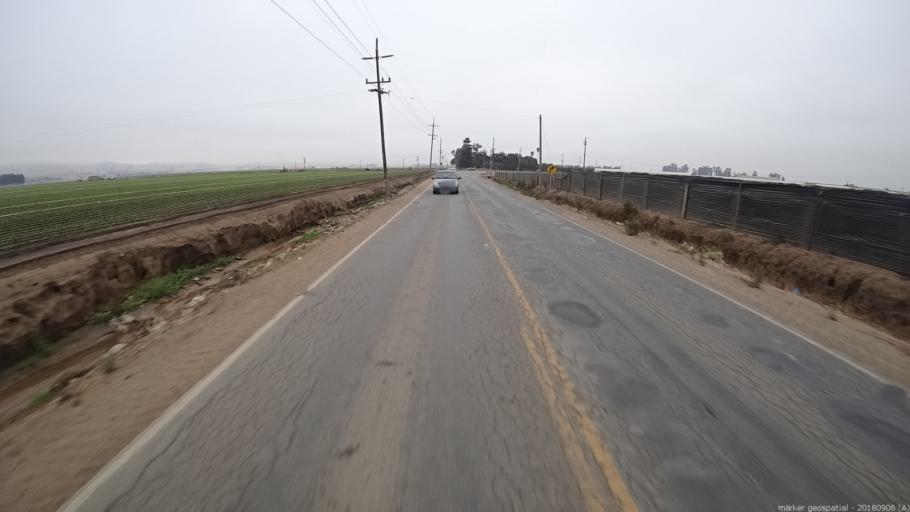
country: US
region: California
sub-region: Monterey County
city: Chualar
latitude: 36.6273
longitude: -121.5322
